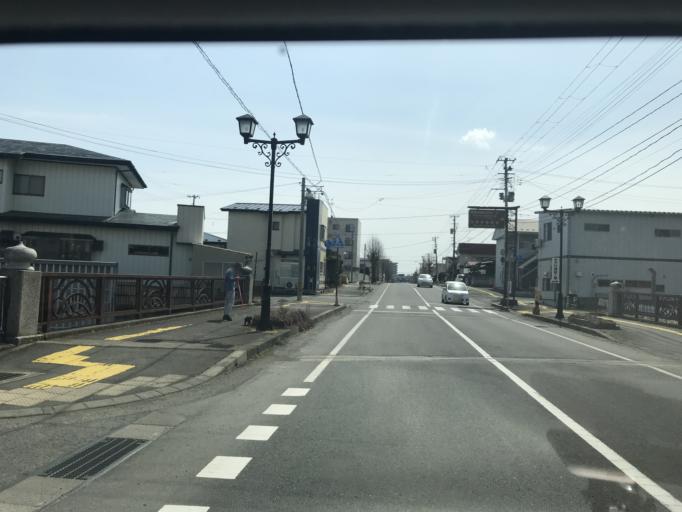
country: JP
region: Iwate
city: Mizusawa
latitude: 39.1314
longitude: 141.1363
